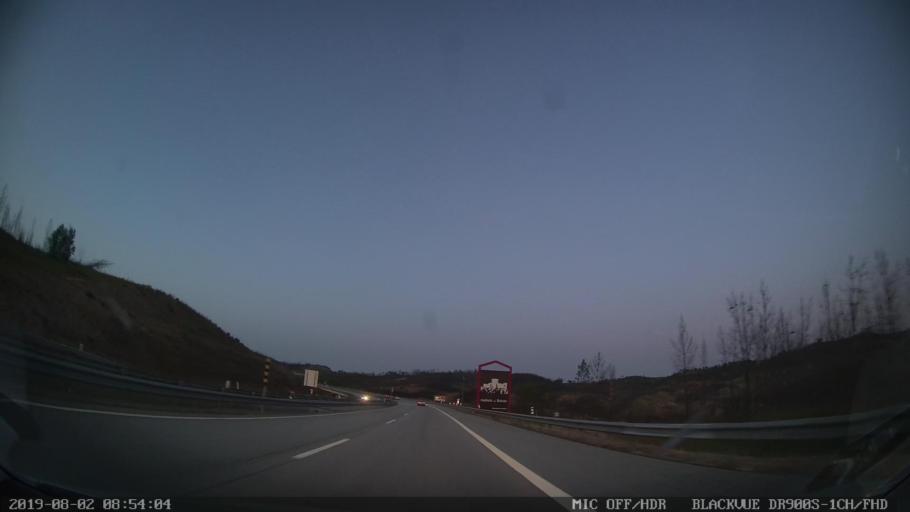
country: PT
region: Santarem
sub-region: Macao
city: Macao
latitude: 39.5230
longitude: -7.9798
